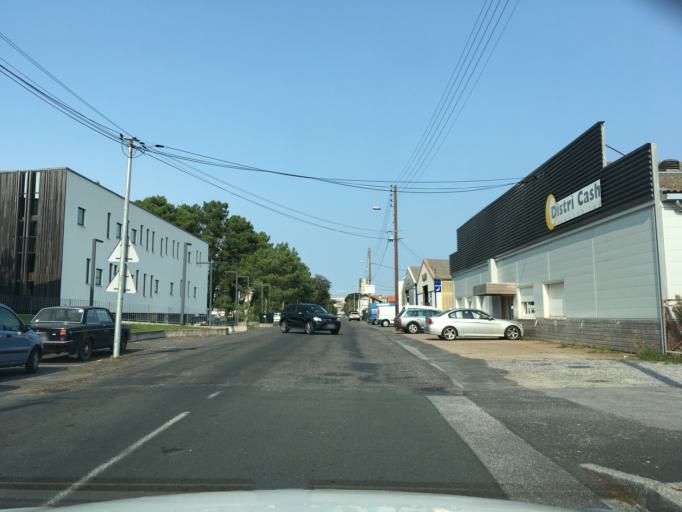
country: FR
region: Aquitaine
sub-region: Departement des Pyrenees-Atlantiques
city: Boucau
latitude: 43.5212
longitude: -1.5028
